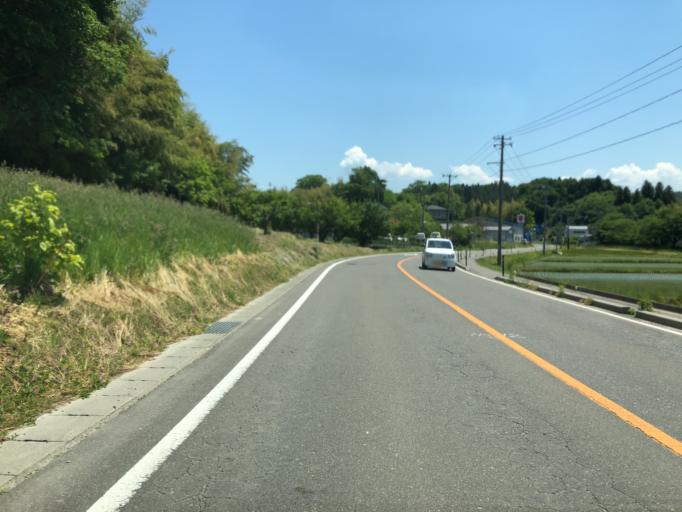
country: JP
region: Fukushima
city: Motomiya
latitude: 37.5002
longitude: 140.4625
